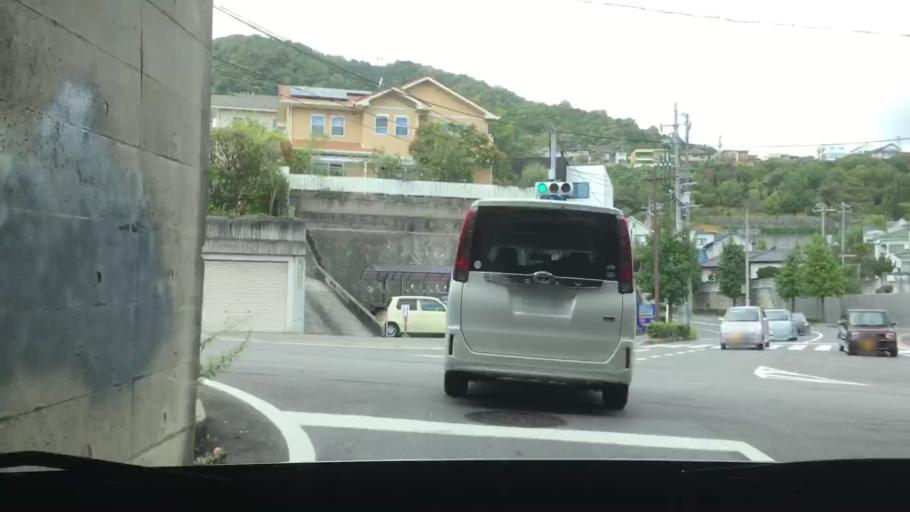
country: JP
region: Hiroshima
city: Hiroshima-shi
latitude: 34.3934
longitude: 132.4131
